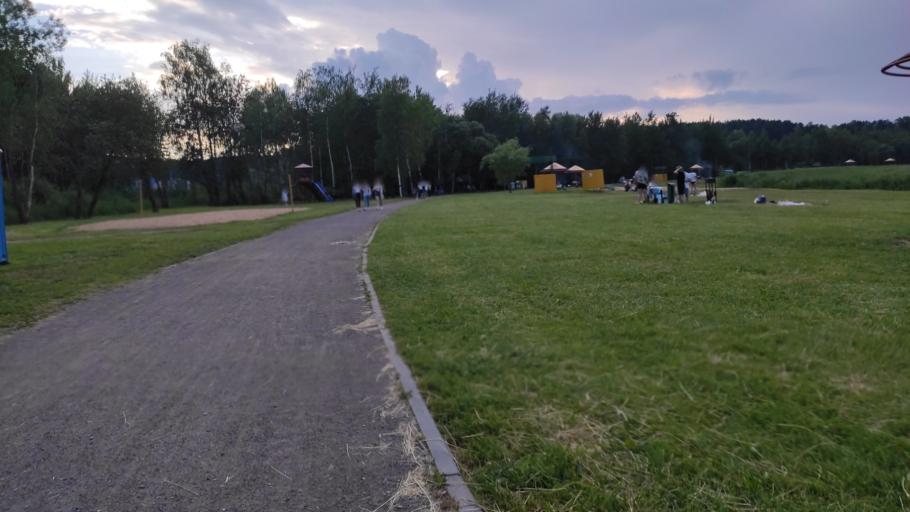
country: BY
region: Minsk
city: Zhdanovichy
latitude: 53.9562
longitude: 27.4480
